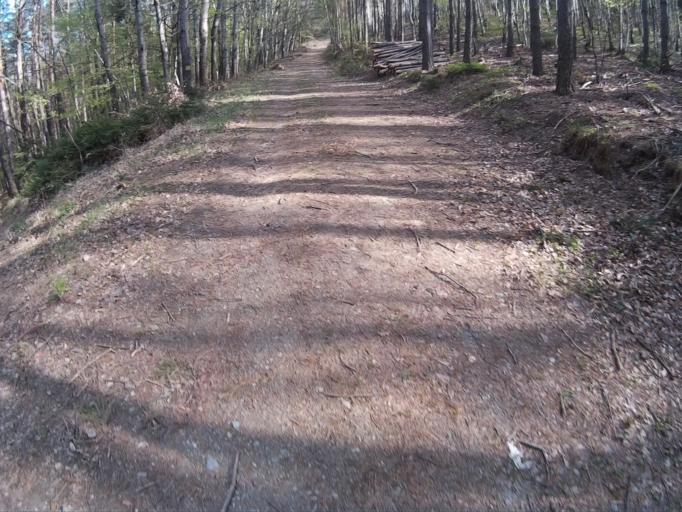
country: AT
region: Burgenland
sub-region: Politischer Bezirk Oberwart
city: Rechnitz
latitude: 47.3381
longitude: 16.4604
